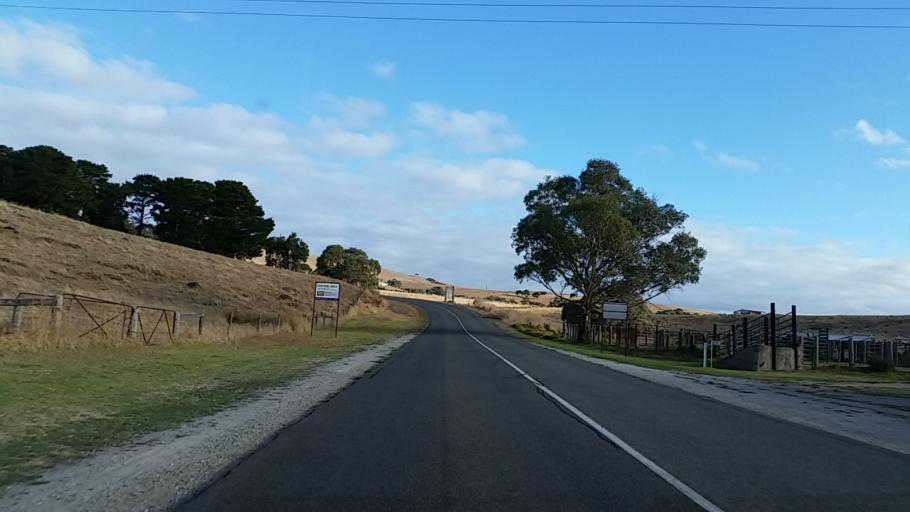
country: AU
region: South Australia
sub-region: Yankalilla
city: Normanville
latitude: -35.5086
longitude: 138.2617
